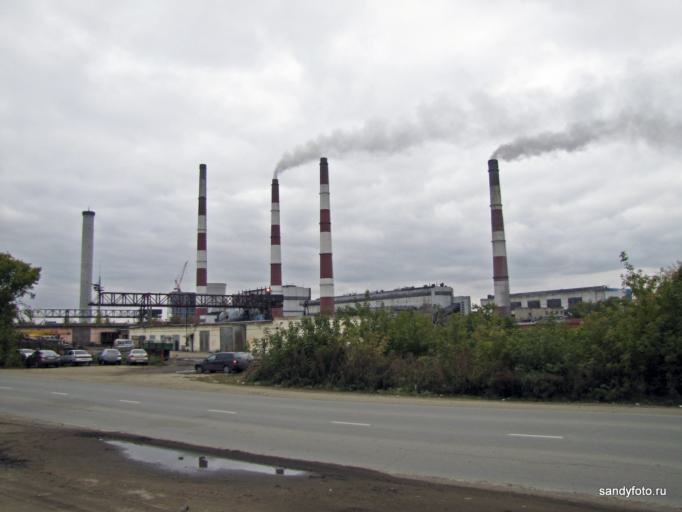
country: RU
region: Chelyabinsk
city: Troitsk
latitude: 54.0415
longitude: 61.6427
